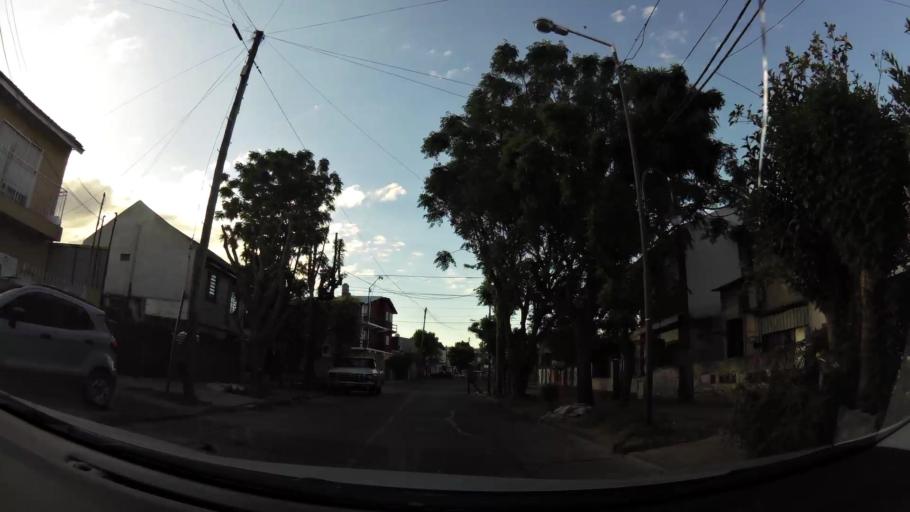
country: AR
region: Buenos Aires
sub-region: Partido de Tigre
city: Tigre
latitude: -34.4556
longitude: -58.5693
